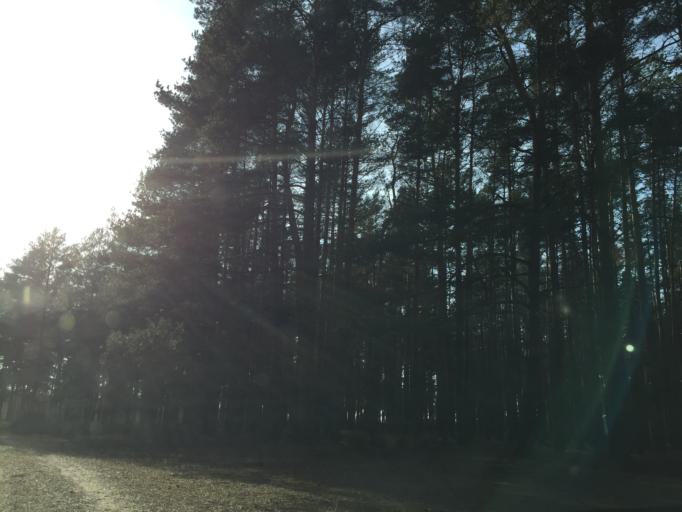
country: LV
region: Adazi
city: Adazi
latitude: 57.1200
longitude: 24.3416
